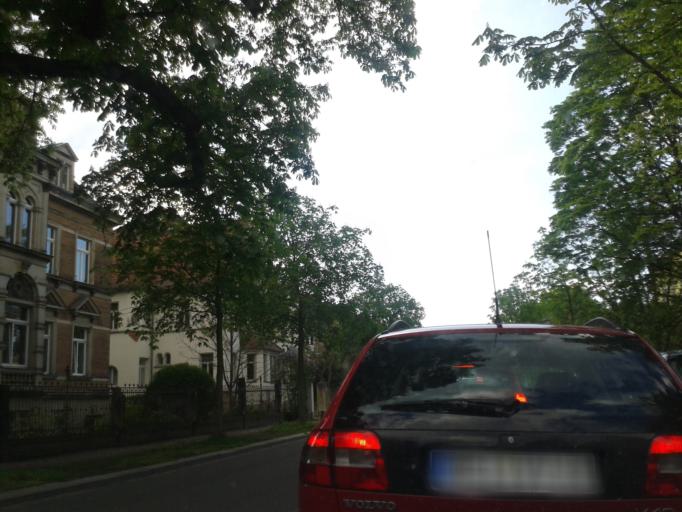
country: DE
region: Saxony
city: Dresden
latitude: 51.0344
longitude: 13.7534
